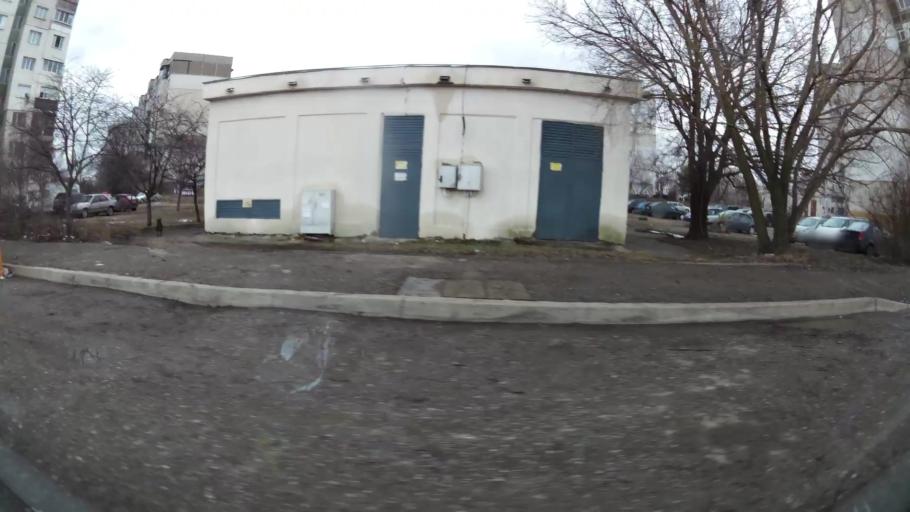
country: BG
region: Sofia-Capital
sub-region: Stolichna Obshtina
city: Sofia
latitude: 42.7368
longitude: 23.2855
